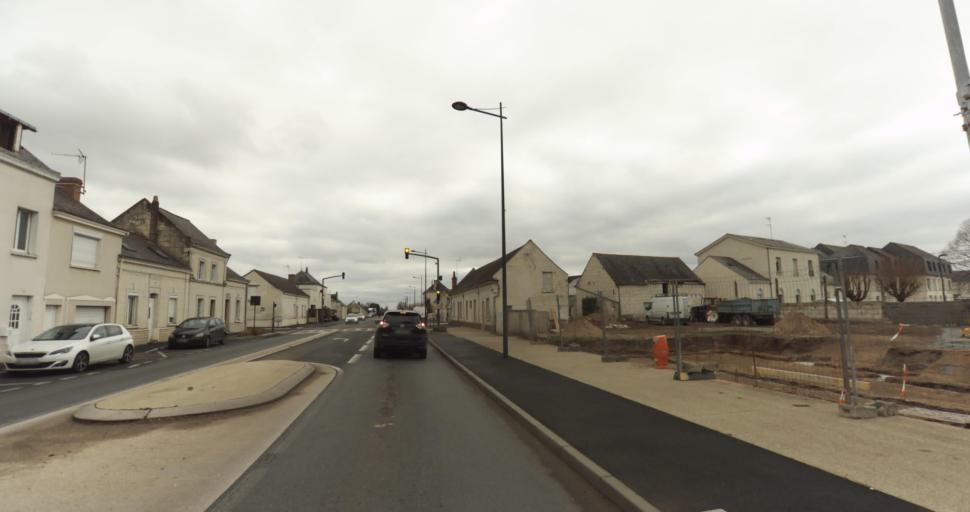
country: FR
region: Pays de la Loire
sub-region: Departement de Maine-et-Loire
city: Vivy
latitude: 47.3244
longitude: -0.0546
